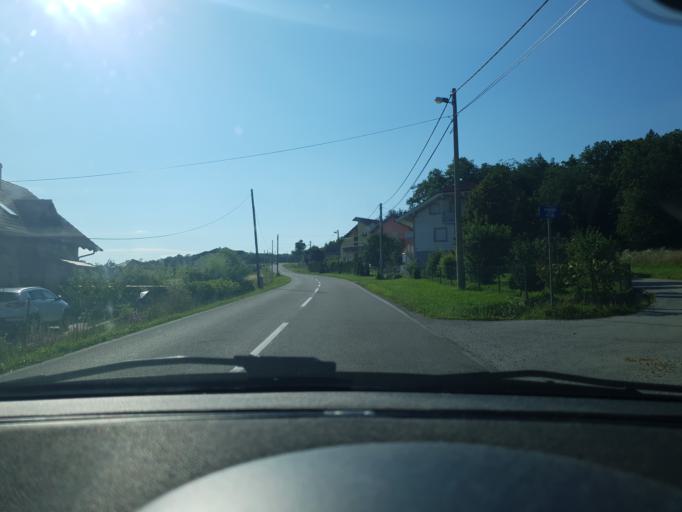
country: HR
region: Zagrebacka
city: Jablanovec
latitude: 45.9120
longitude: 15.8509
